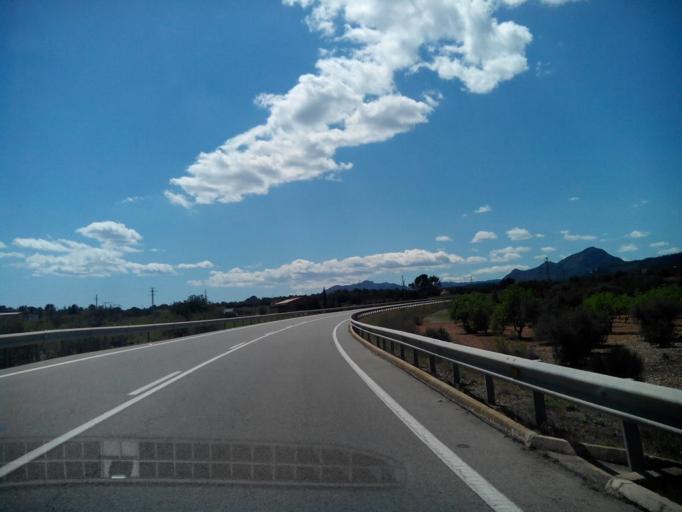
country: ES
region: Catalonia
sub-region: Provincia de Tarragona
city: Vilanova d'Escornalbou
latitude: 41.0843
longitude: 0.9681
